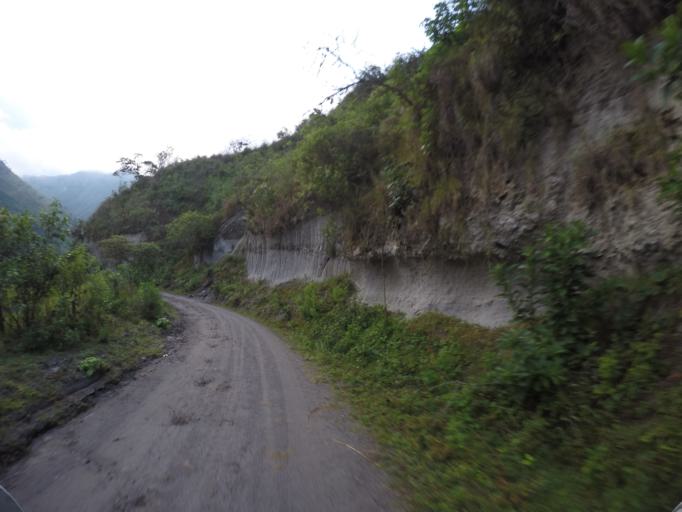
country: CO
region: Tolima
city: Cajamarca
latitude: 4.5193
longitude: -75.4074
